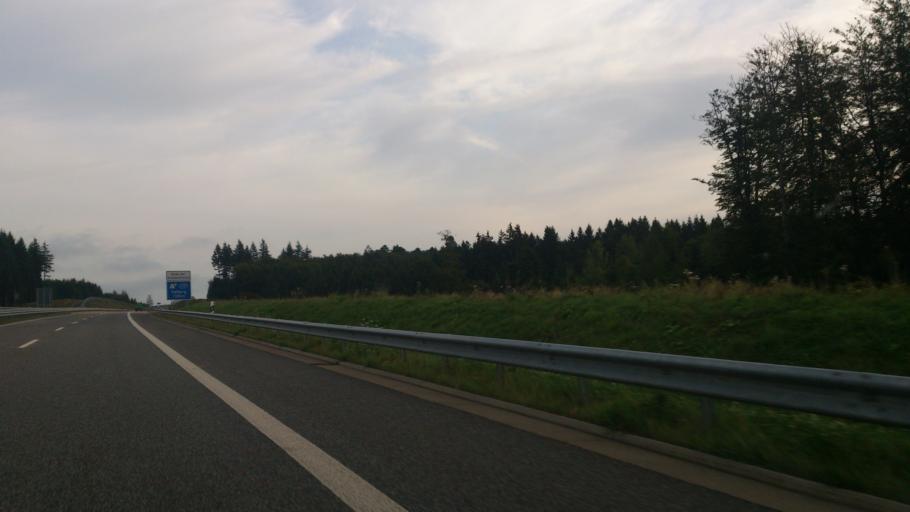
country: DE
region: Rheinland-Pfalz
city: Kradenbach
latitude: 50.2558
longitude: 6.8258
